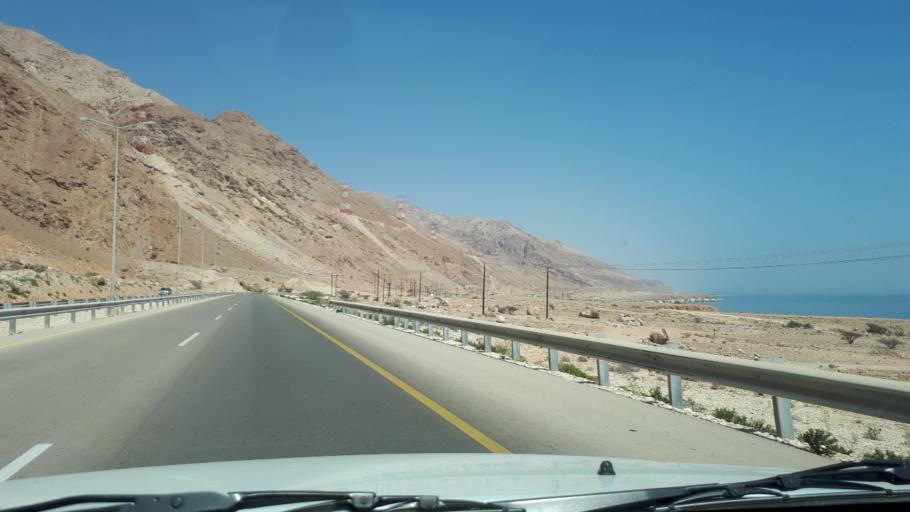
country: OM
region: Ash Sharqiyah
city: Sur
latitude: 22.7596
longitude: 59.2941
